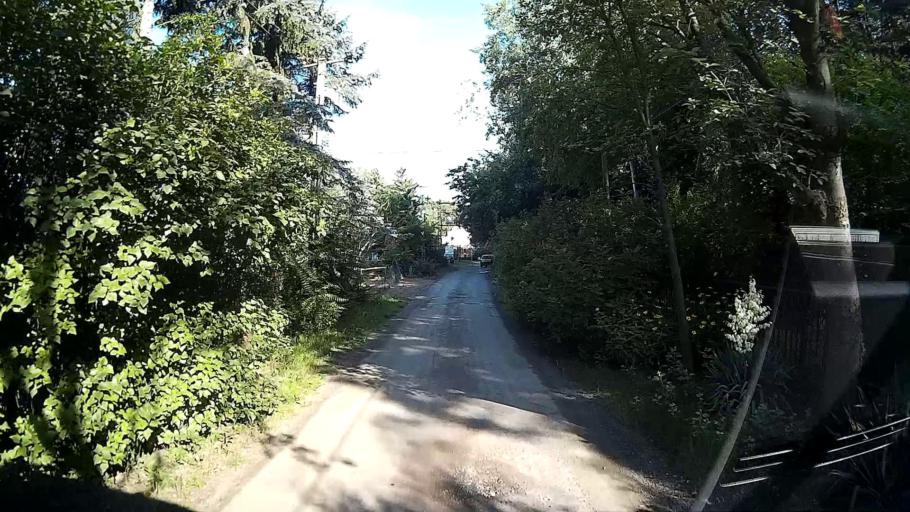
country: HU
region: Pest
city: God
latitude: 47.6795
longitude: 19.1145
